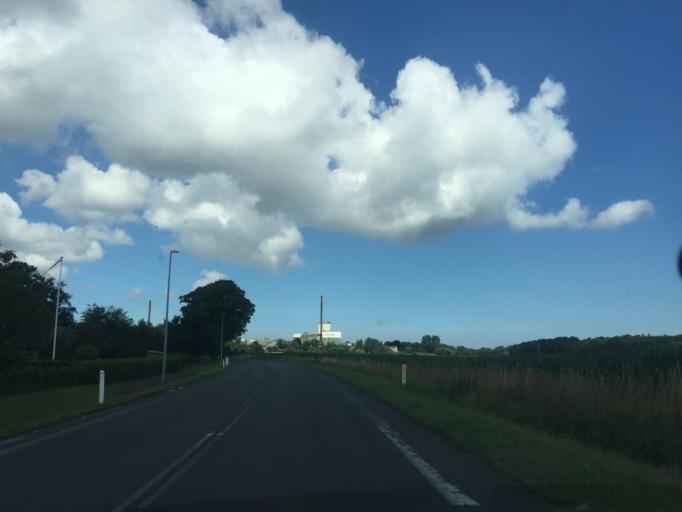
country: DK
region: South Denmark
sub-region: Nordfyns Kommune
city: Otterup
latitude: 55.5298
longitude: 10.3897
